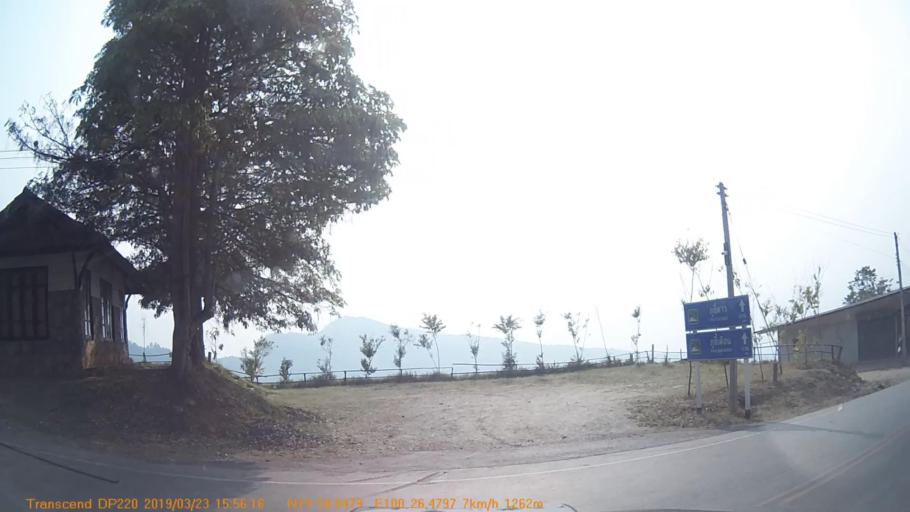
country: TH
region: Chiang Rai
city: Khun Tan
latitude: 19.8474
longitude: 100.4414
